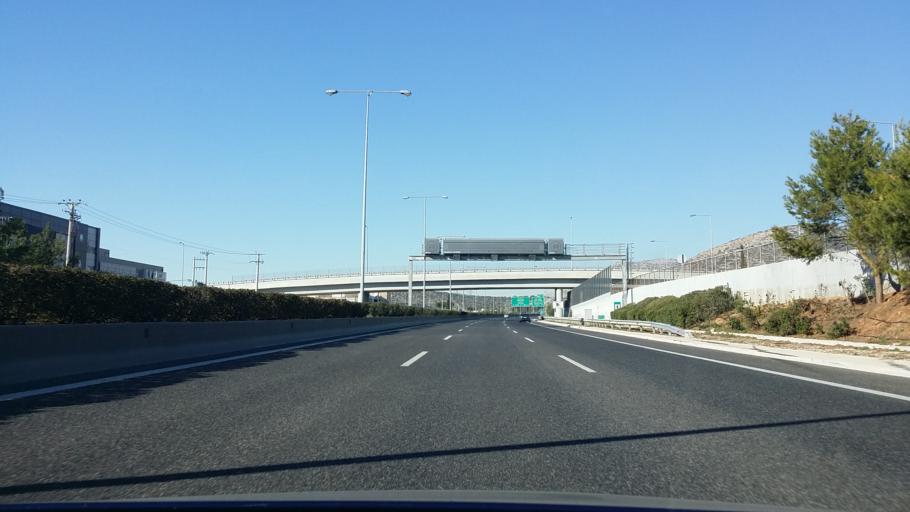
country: GR
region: Attica
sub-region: Nomarchia Dytikis Attikis
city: Ano Liosia
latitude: 38.0747
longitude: 23.6873
